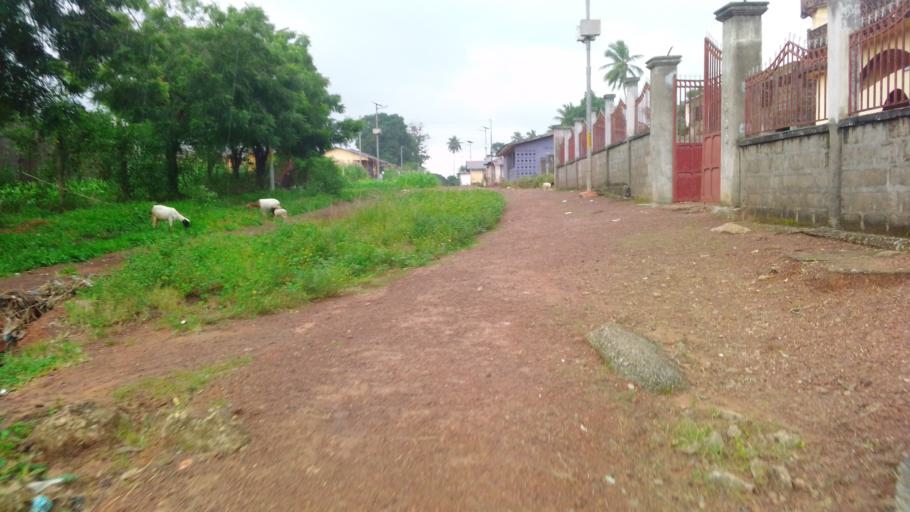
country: SL
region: Northern Province
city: Lunsar
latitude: 8.6822
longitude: -12.5328
